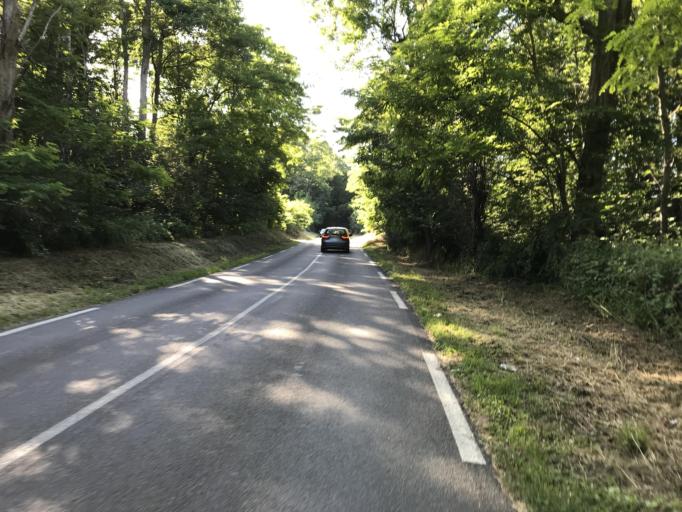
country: FR
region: Ile-de-France
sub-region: Departement de l'Essonne
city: Villejust
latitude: 48.6837
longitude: 2.2450
